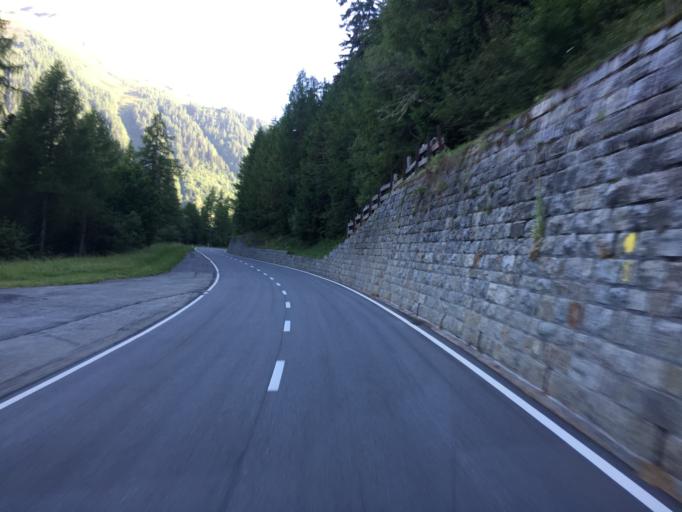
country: CH
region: Valais
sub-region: Martigny District
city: Martigny-Combe
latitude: 46.0690
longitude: 7.0175
